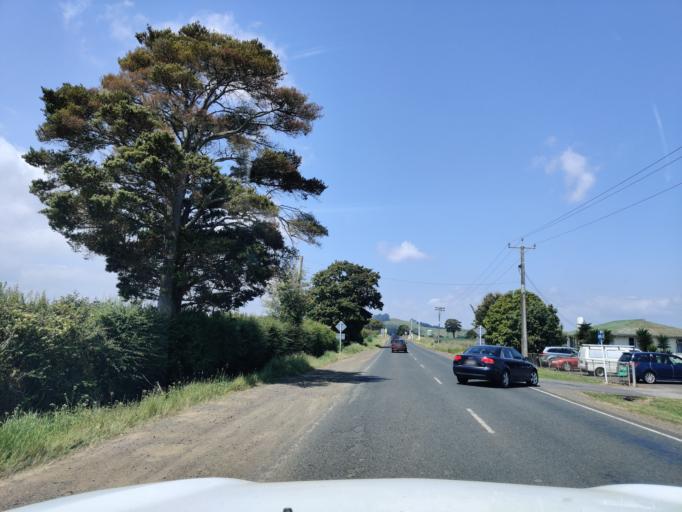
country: NZ
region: Auckland
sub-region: Auckland
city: Pukekohe East
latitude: -37.2394
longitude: 174.9523
